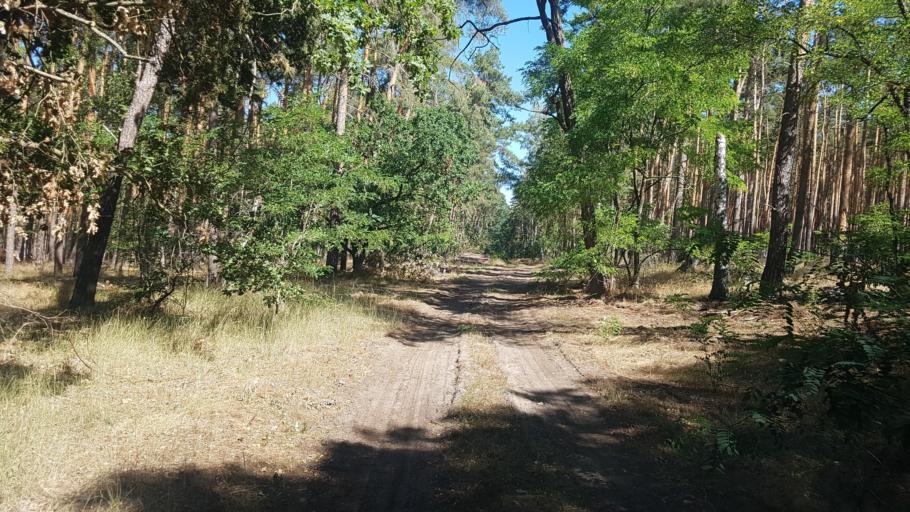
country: DE
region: Brandenburg
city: Golzow
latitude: 52.3067
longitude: 12.5647
